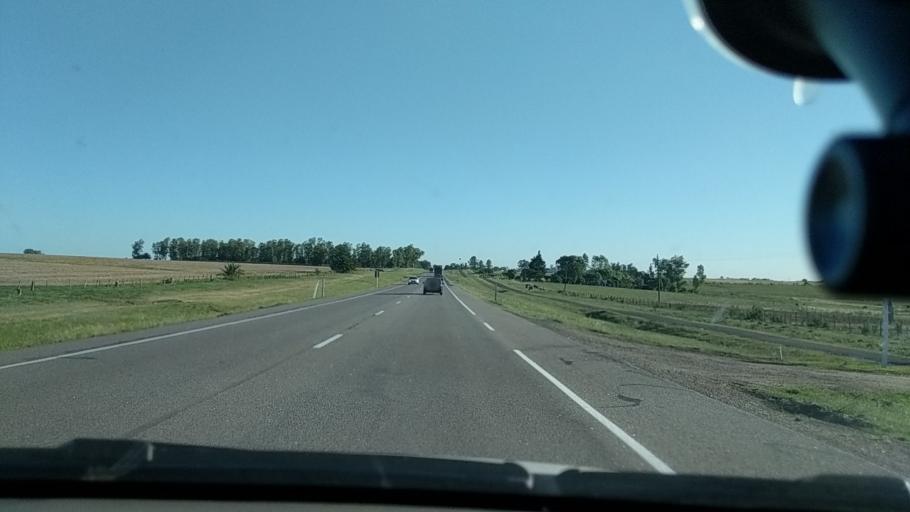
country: UY
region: Florida
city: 25 de Mayo
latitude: -34.2612
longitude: -56.2139
